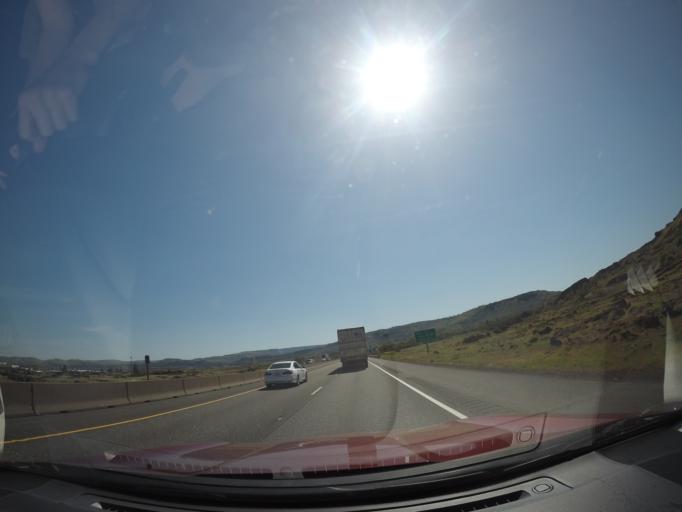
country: US
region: Oregon
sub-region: Wasco County
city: Chenoweth
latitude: 45.6376
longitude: -121.2100
